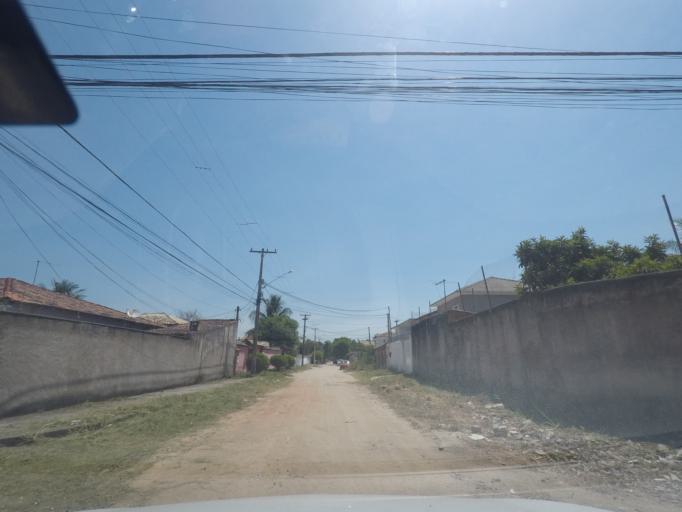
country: BR
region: Rio de Janeiro
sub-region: Niteroi
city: Niteroi
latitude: -22.9356
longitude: -43.0167
